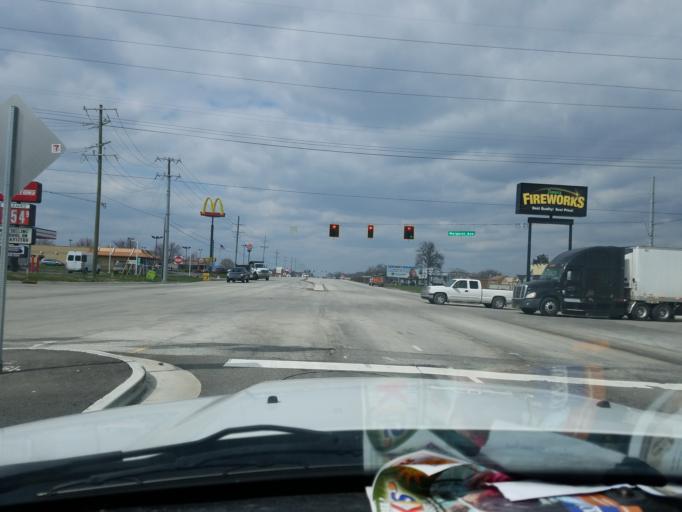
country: US
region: Indiana
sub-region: Vigo County
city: Terre Haute
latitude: 39.4335
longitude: -87.3329
